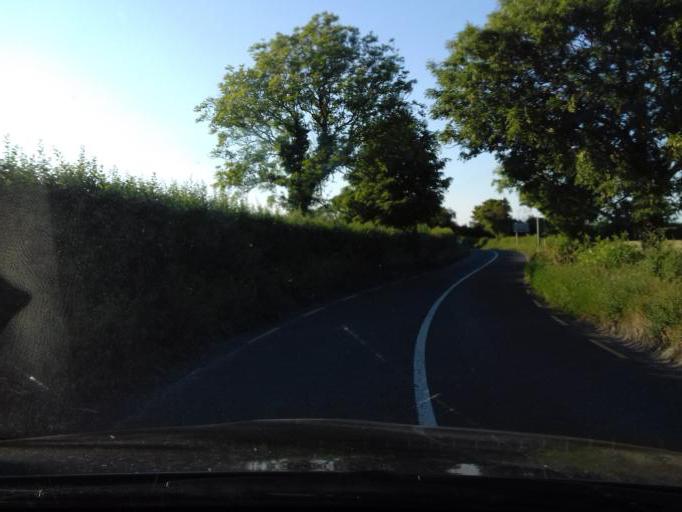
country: IE
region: Leinster
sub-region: An Mhi
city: Ashbourne
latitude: 53.5391
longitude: -6.3684
